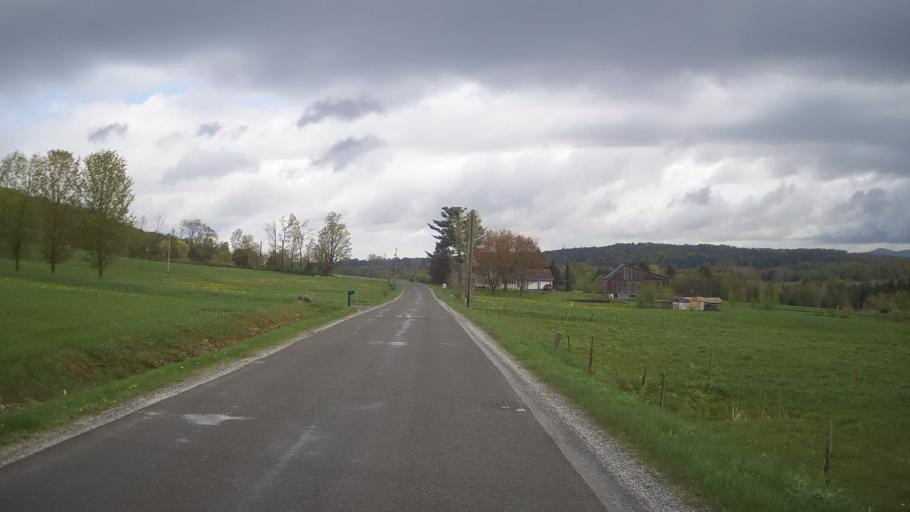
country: CA
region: Quebec
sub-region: Monteregie
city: Cowansville
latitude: 45.1873
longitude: -72.6979
